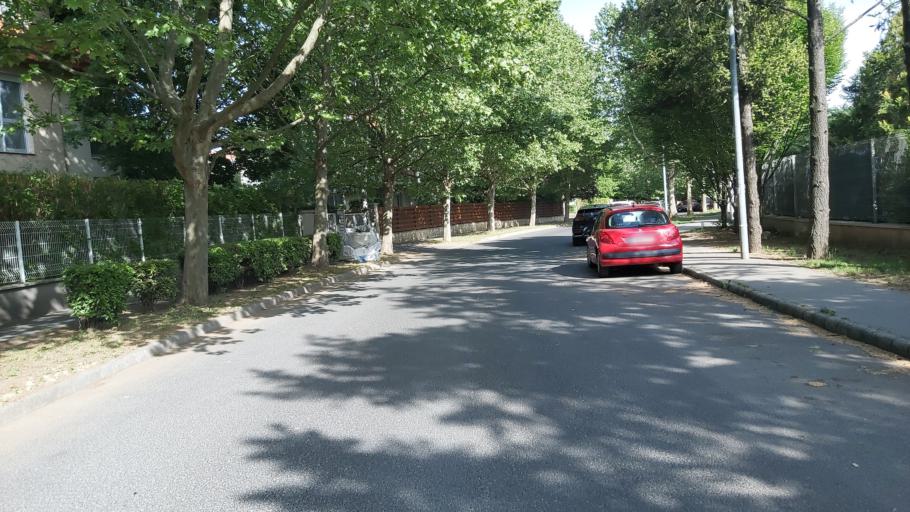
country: HU
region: Budapest
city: Budapest XXII. keruelet
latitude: 47.4462
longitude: 19.0074
